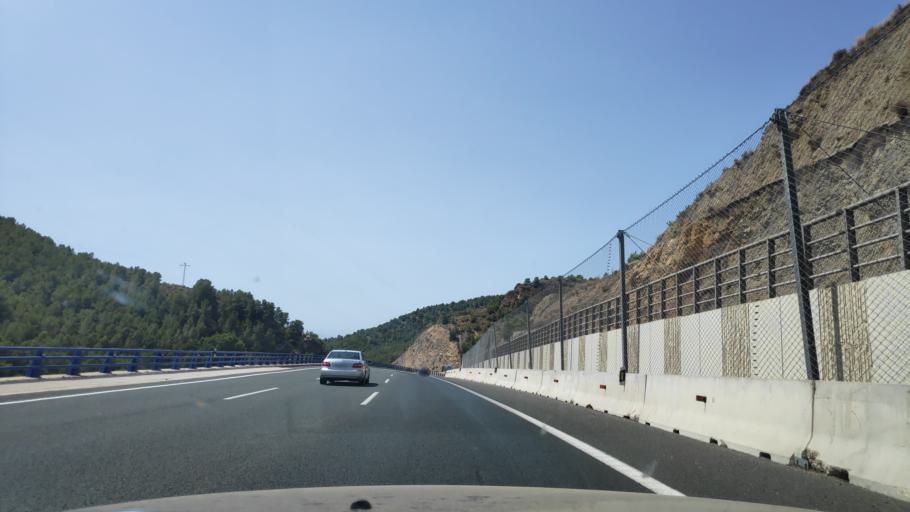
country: ES
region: Murcia
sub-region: Murcia
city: Murcia
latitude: 37.9027
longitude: -1.1440
